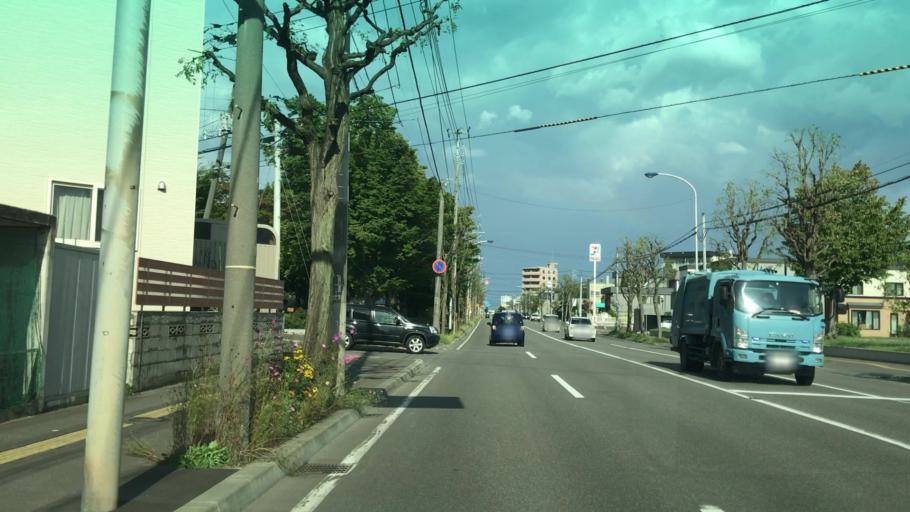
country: JP
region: Hokkaido
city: Sapporo
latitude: 43.0844
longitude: 141.2990
